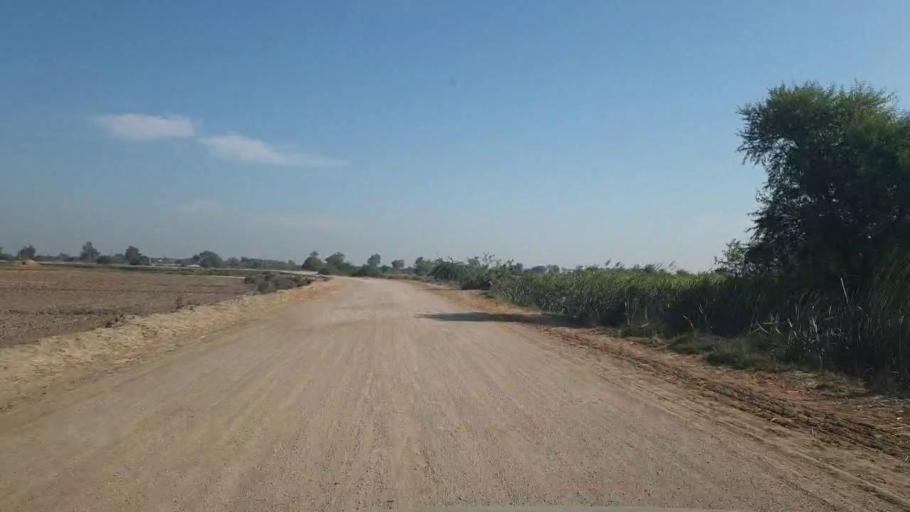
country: PK
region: Sindh
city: Rajo Khanani
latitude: 24.9727
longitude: 68.7760
